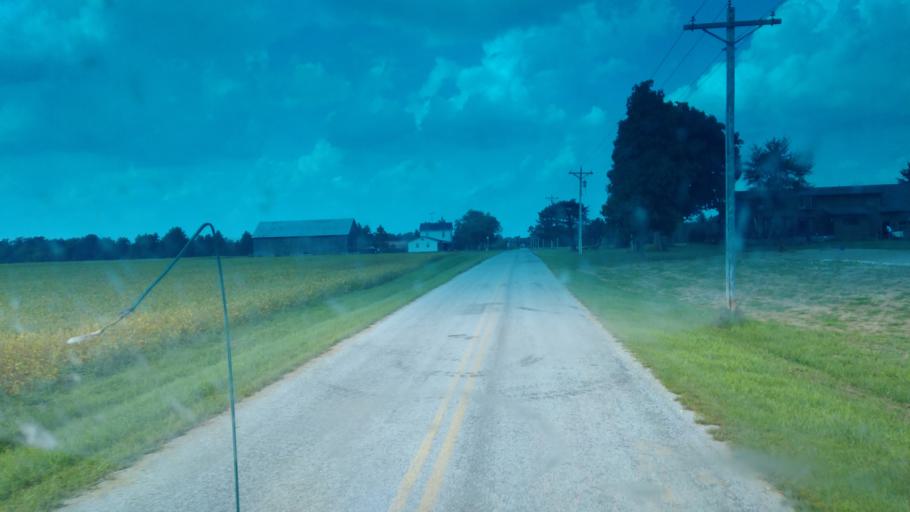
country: US
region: Ohio
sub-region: Hardin County
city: Kenton
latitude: 40.7387
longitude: -83.6015
